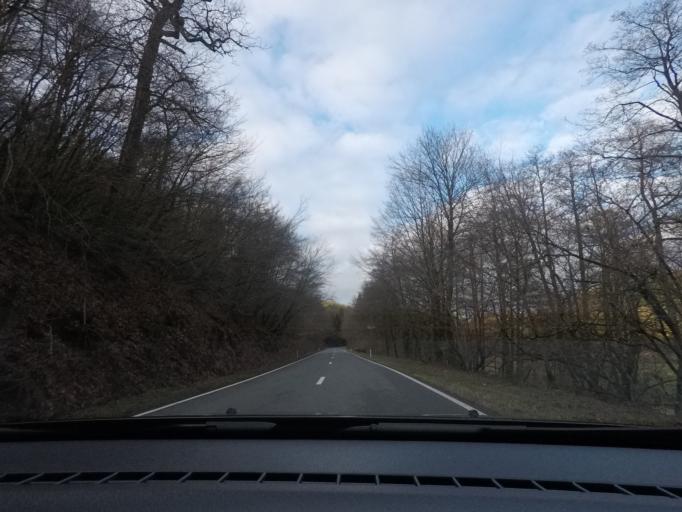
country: BE
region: Wallonia
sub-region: Province du Luxembourg
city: Leglise
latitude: 49.7416
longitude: 5.5272
